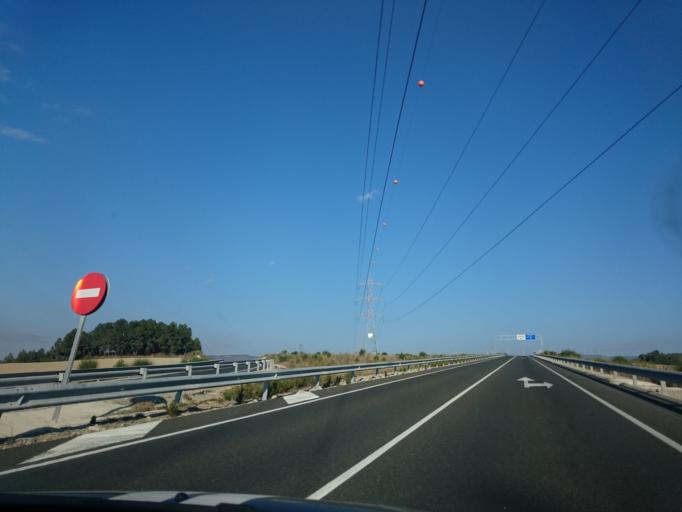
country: ES
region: Catalonia
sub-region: Provincia de Barcelona
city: Odena
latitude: 41.5871
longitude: 1.6640
